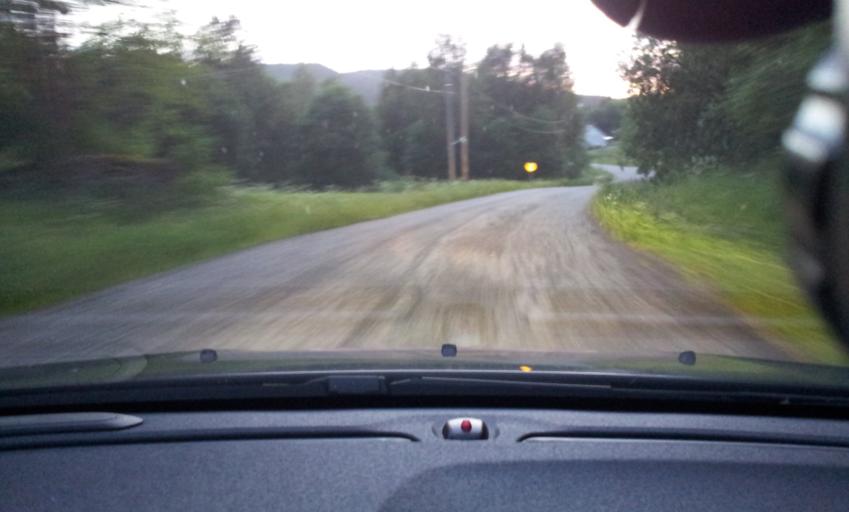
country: SE
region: Vaesternorrland
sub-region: Ange Kommun
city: Fransta
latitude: 62.7798
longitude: 16.0054
